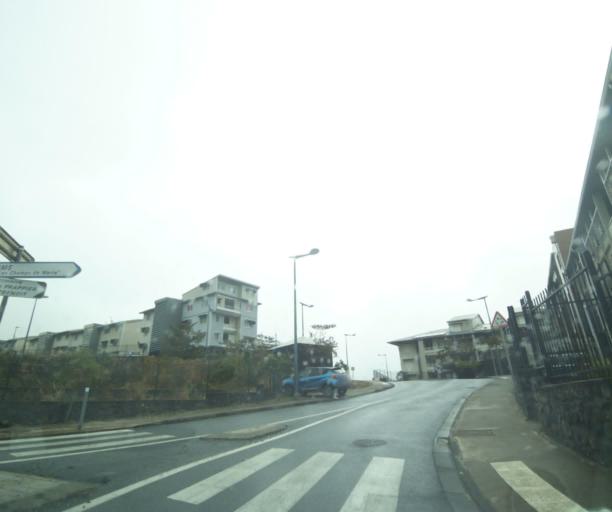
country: RE
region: Reunion
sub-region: Reunion
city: Saint-Paul
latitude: -21.0459
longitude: 55.2599
